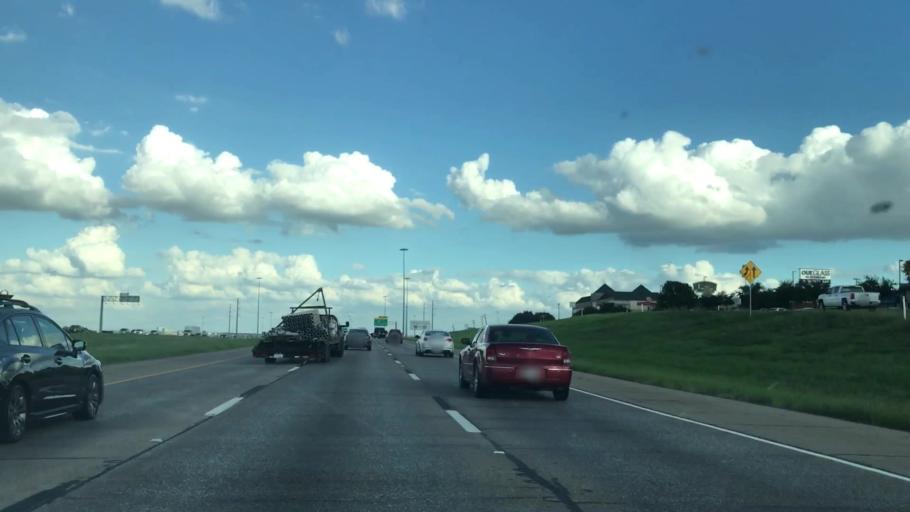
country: US
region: Texas
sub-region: Dallas County
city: Farmers Branch
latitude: 32.9145
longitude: -96.9559
